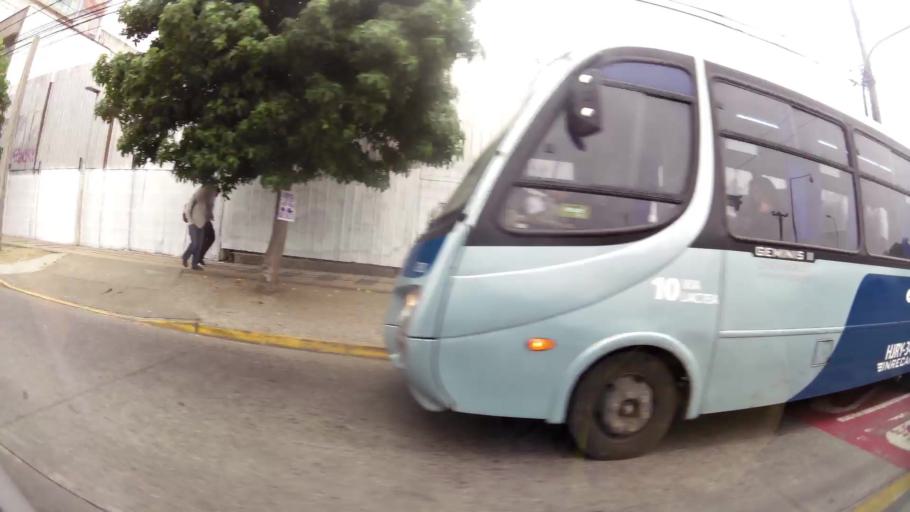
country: CL
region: Biobio
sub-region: Provincia de Concepcion
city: Concepcion
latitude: -36.8338
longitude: -73.0563
